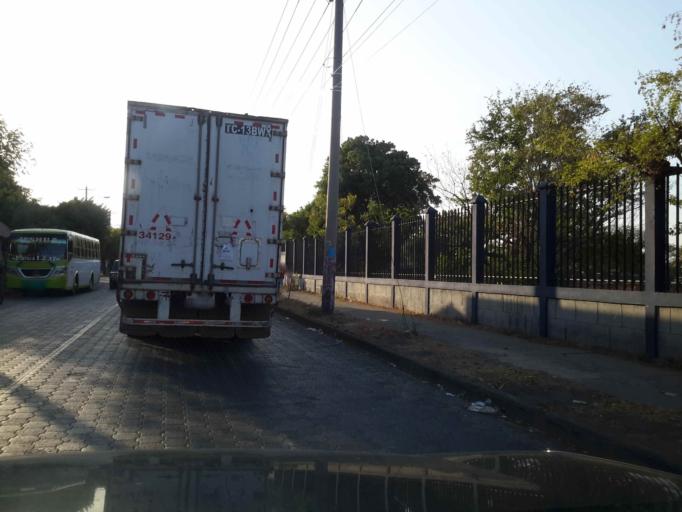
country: NI
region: Managua
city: Ciudad Sandino
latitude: 12.1579
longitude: -86.2954
